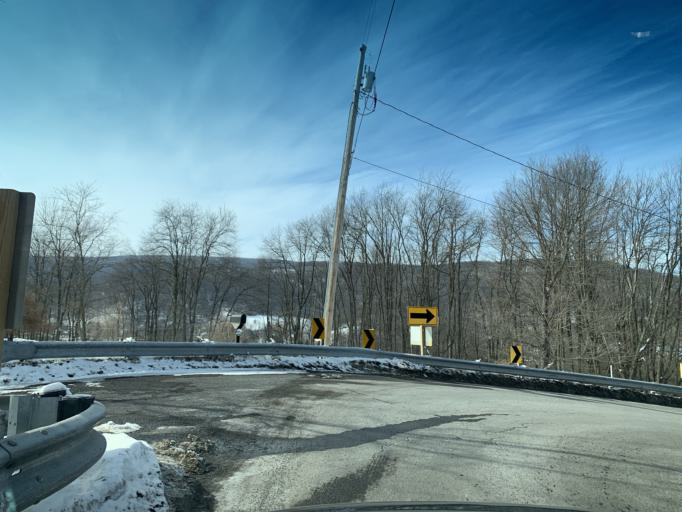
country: US
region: Maryland
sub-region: Allegany County
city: Frostburg
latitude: 39.6729
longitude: -78.8937
